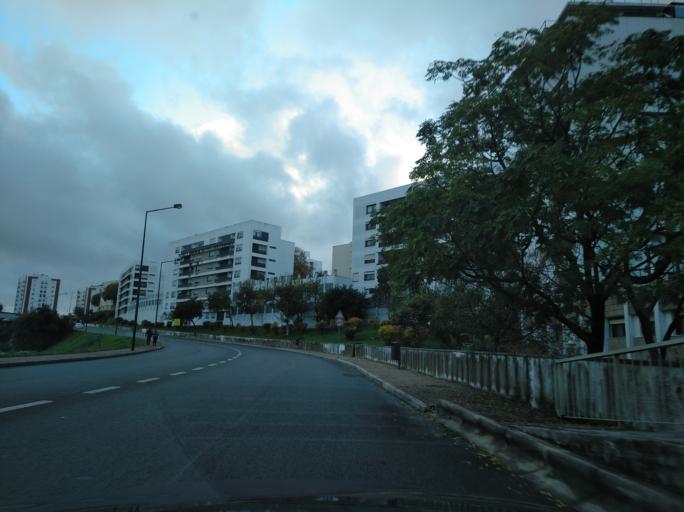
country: PT
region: Lisbon
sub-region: Loures
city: Moscavide
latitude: 38.7465
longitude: -9.1101
